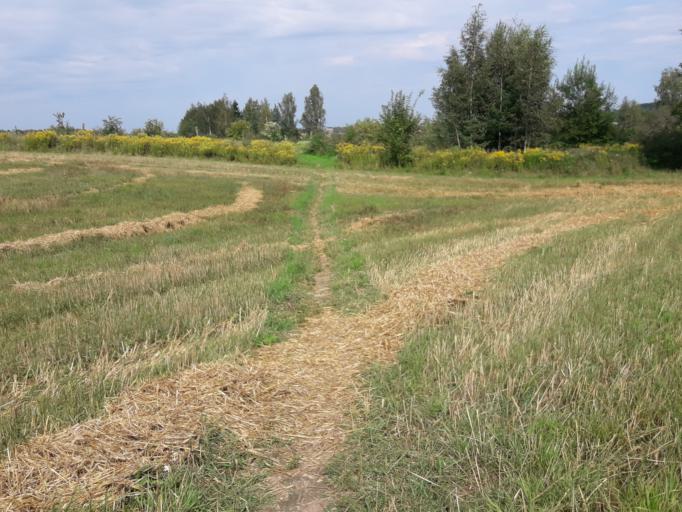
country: BY
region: Minsk
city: Pyatryshki
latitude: 54.1279
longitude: 27.1311
